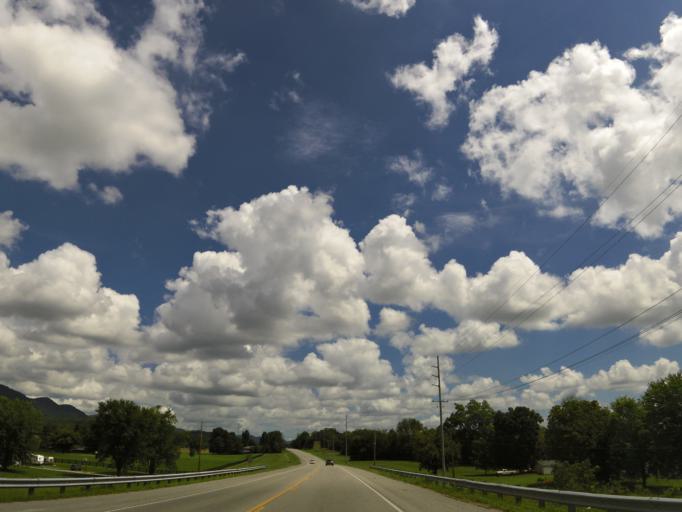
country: US
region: Kentucky
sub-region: Bell County
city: Middlesboro
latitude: 36.4961
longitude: -83.8117
